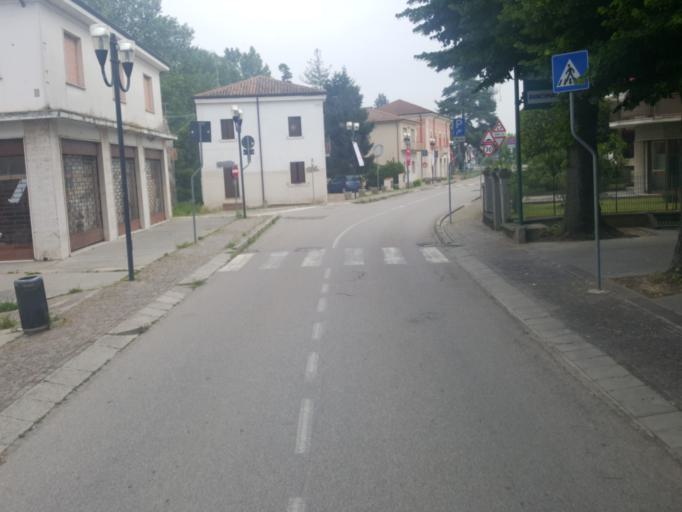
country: IT
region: Veneto
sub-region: Provincia di Rovigo
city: Canaro
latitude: 44.9344
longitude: 11.6760
